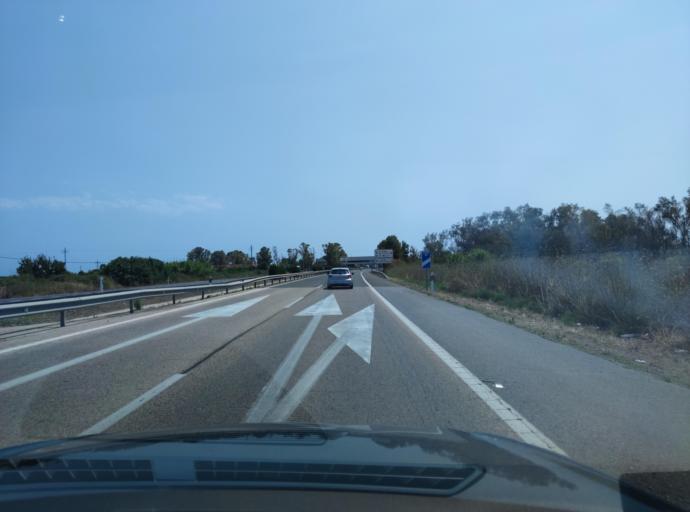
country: ES
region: Valencia
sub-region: Provincia de Castello
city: Alquerias del Nino Perdido
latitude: 39.8695
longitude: -0.1222
